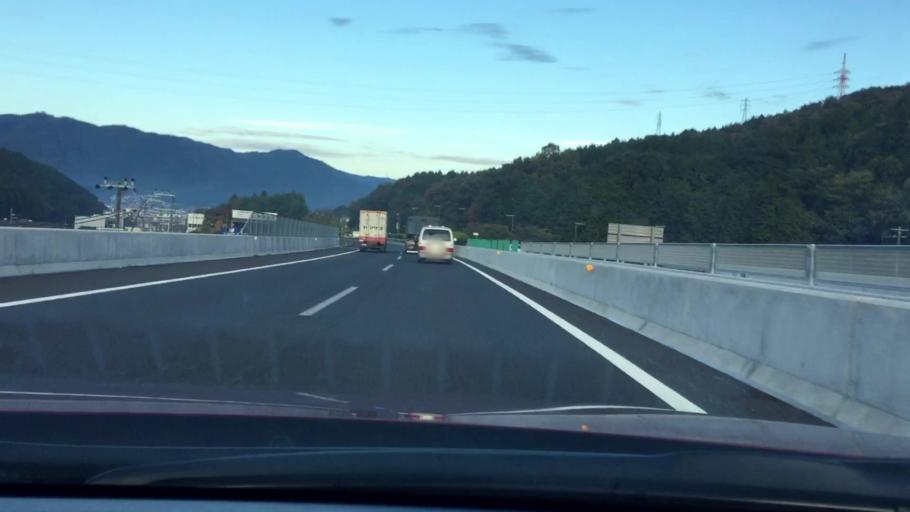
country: JP
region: Hyogo
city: Yamazakicho-nakabirose
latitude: 34.9938
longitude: 134.5715
